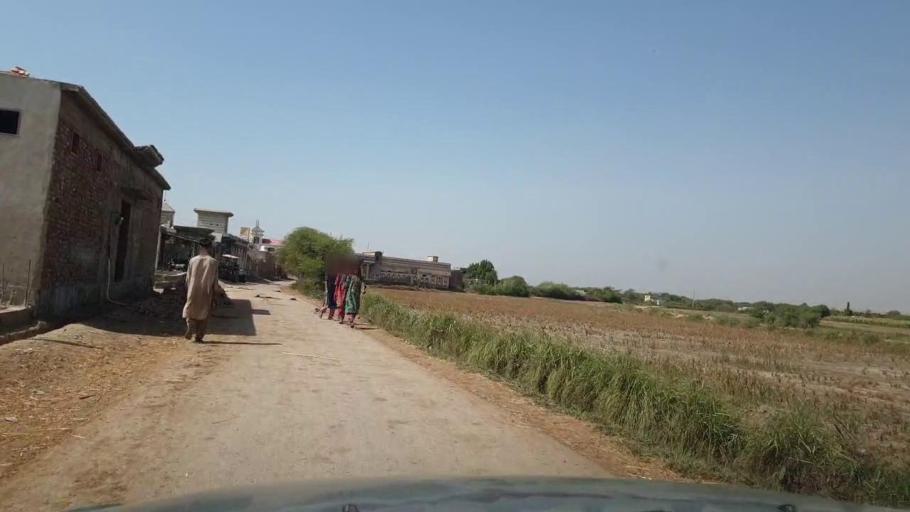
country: PK
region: Sindh
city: Tando Muhammad Khan
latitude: 25.1493
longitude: 68.4379
